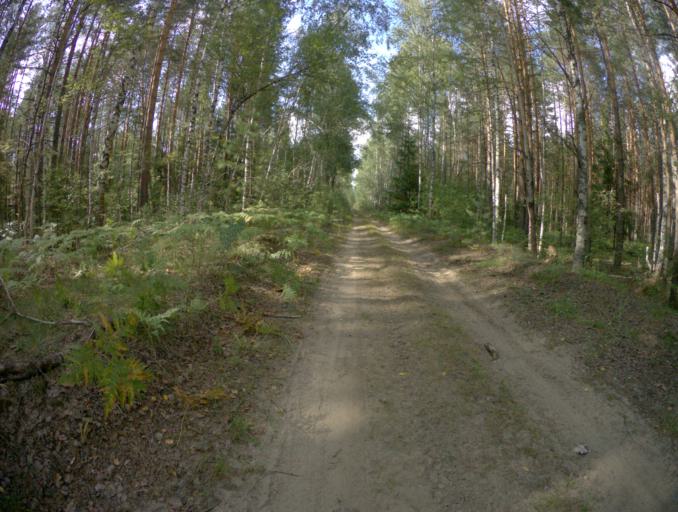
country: RU
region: Vladimir
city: Sobinka
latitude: 55.9245
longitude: 40.0663
